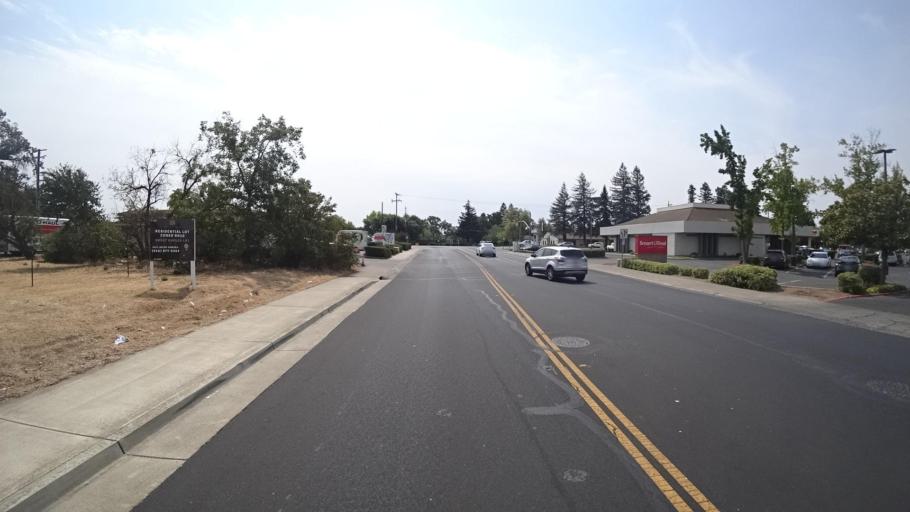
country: US
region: California
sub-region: Sacramento County
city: Elk Grove
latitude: 38.4098
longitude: -121.3761
